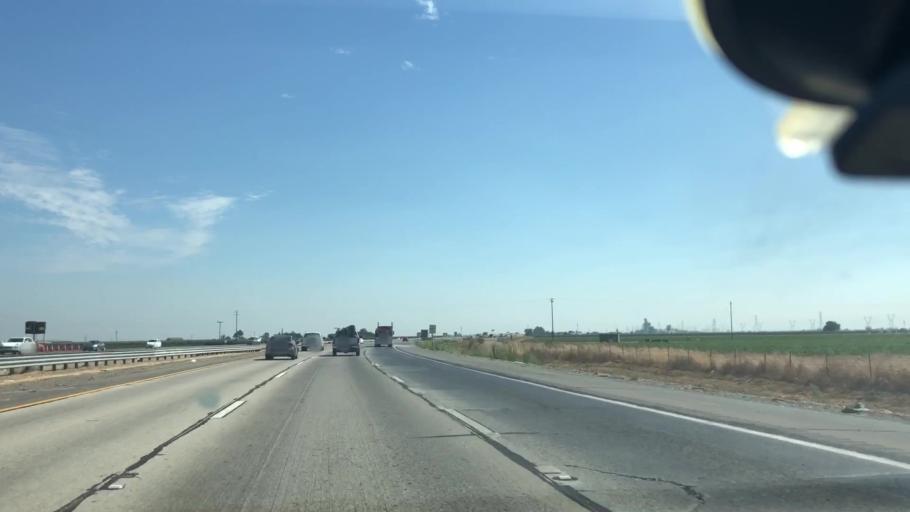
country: US
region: California
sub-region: San Joaquin County
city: Woodbridge
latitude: 38.1095
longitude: -121.3937
